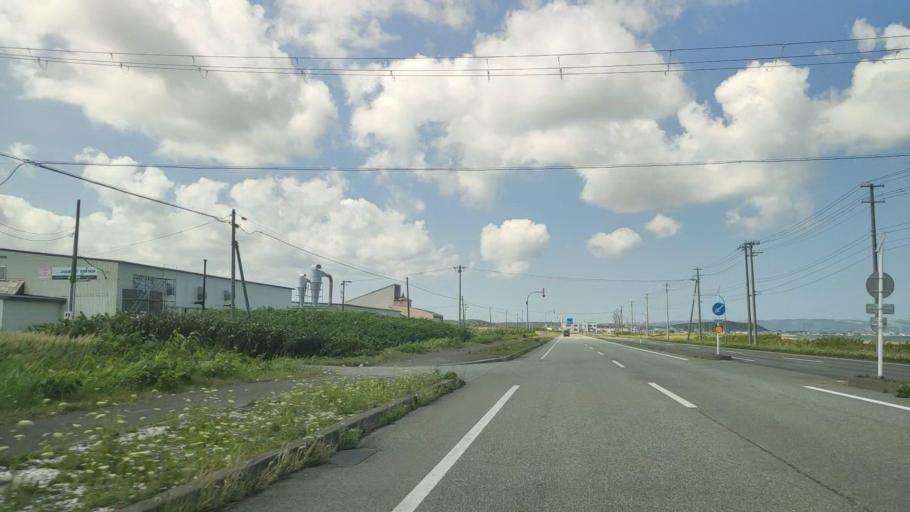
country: JP
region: Hokkaido
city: Makubetsu
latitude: 45.4041
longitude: 141.7893
